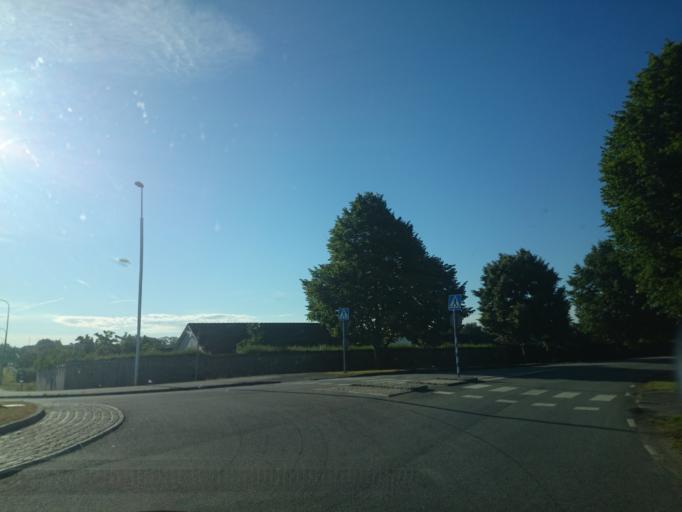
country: SE
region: Skane
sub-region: Eslovs Kommun
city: Eslov
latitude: 55.7251
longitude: 13.3387
